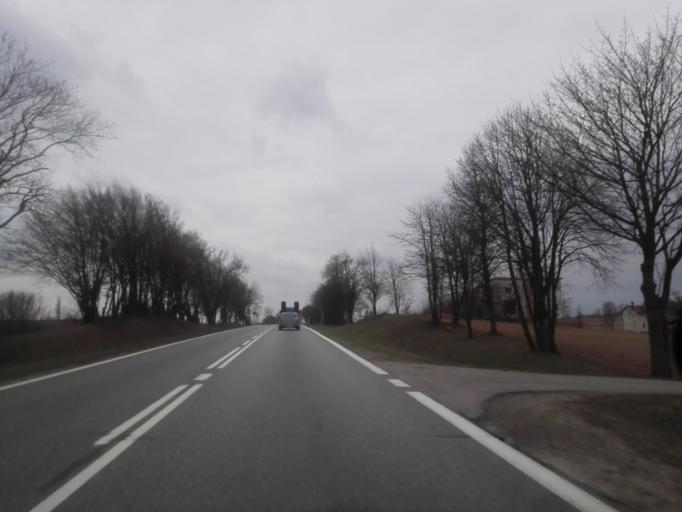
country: PL
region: Podlasie
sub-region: Powiat augustowski
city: Augustow
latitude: 53.8191
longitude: 22.9306
